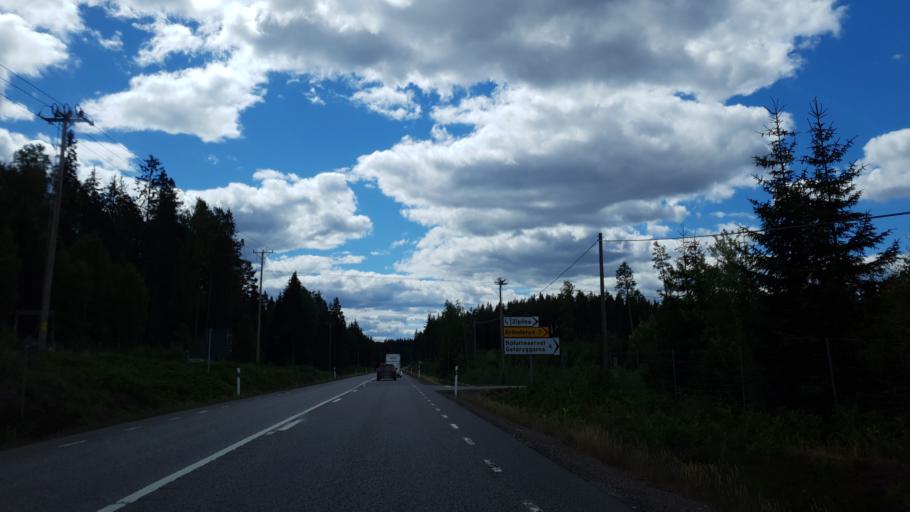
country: SE
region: Kronoberg
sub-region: Vaxjo Kommun
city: Braas
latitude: 57.1803
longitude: 15.1581
